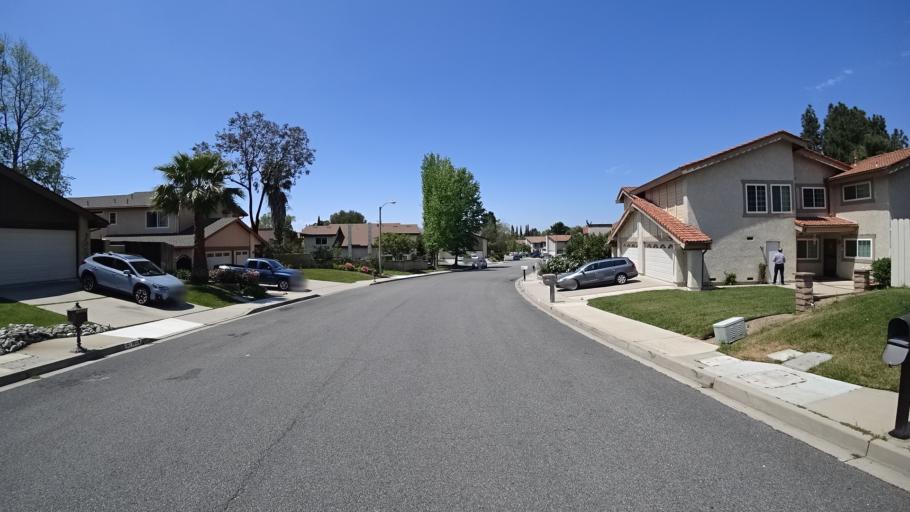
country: US
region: California
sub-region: Ventura County
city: Casa Conejo
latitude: 34.1807
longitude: -118.9184
